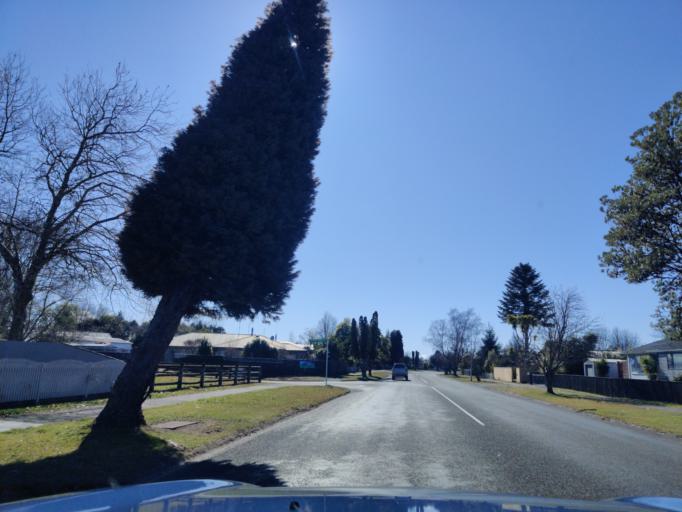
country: NZ
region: Waikato
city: Turangi
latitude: -38.9934
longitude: 175.8037
